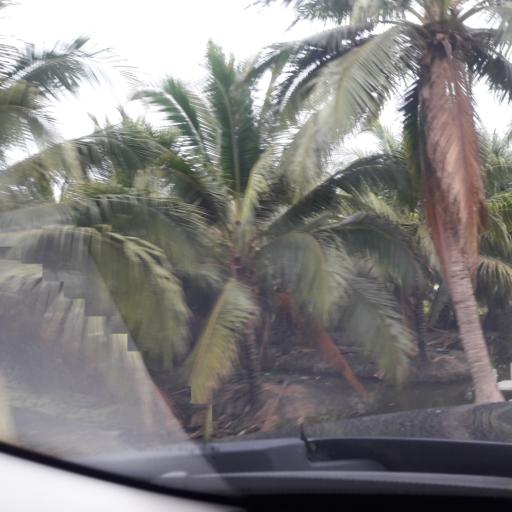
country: TH
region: Ratchaburi
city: Damnoen Saduak
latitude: 13.5594
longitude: 99.9575
